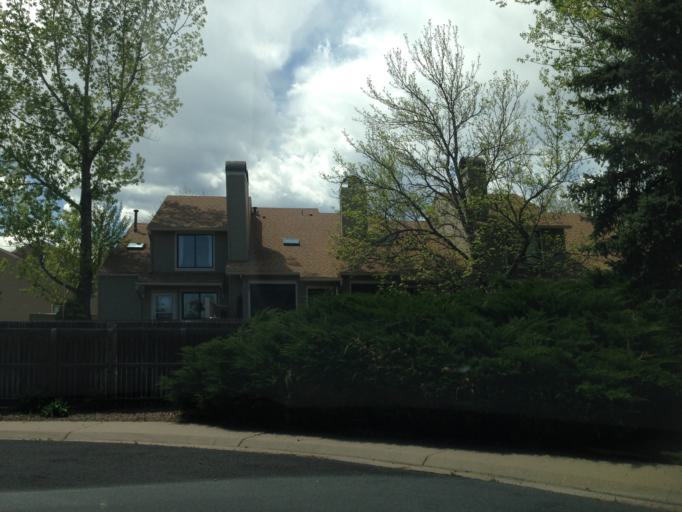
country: US
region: Colorado
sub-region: Boulder County
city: Superior
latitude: 39.9659
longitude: -105.1538
